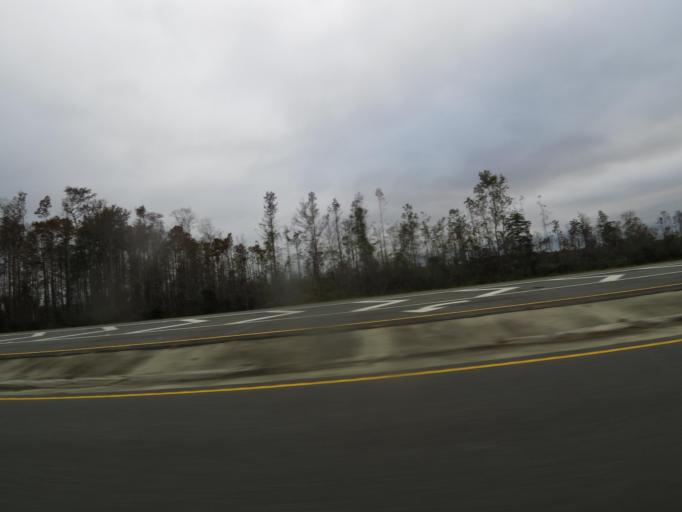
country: US
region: Georgia
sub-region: Charlton County
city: Folkston
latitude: 30.8863
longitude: -82.0428
